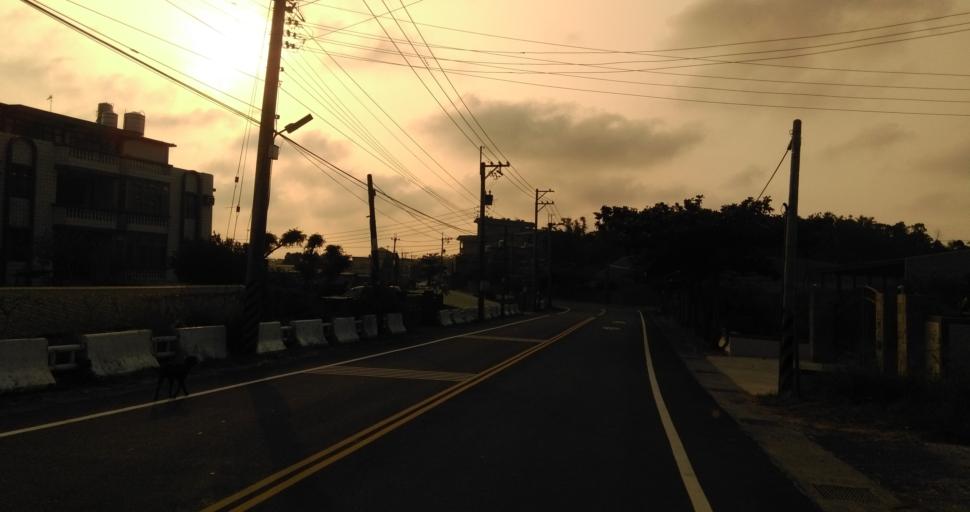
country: TW
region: Taiwan
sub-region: Hsinchu
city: Hsinchu
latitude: 24.7455
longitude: 120.9224
